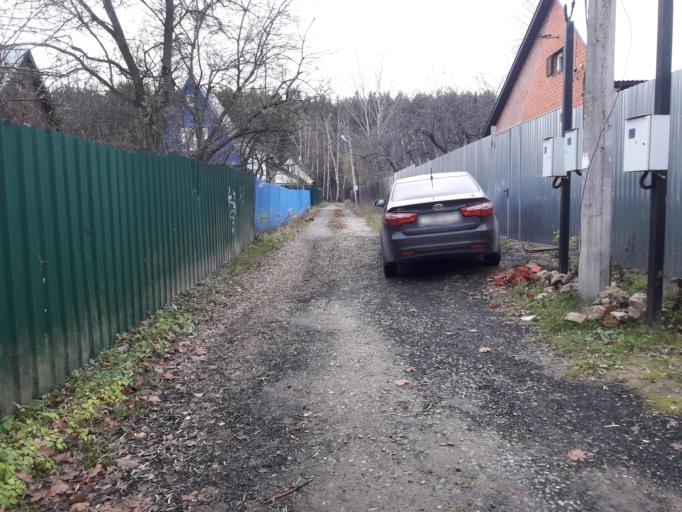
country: RU
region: Moskovskaya
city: Sofrino
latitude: 56.1687
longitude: 37.9292
